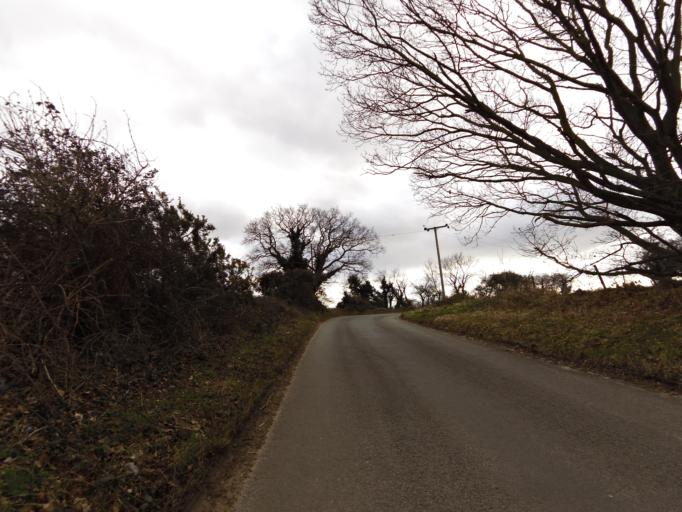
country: GB
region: England
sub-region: Suffolk
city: Woodbridge
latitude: 52.0282
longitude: 1.3071
